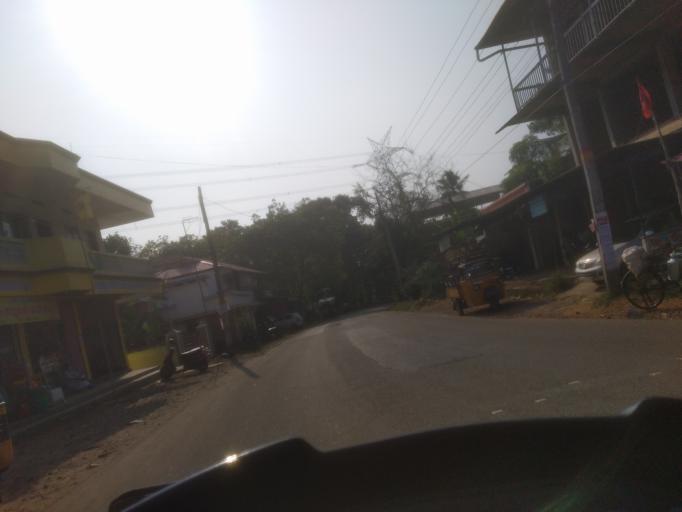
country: IN
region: Kerala
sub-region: Ernakulam
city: Piravam
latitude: 9.8341
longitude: 76.5194
